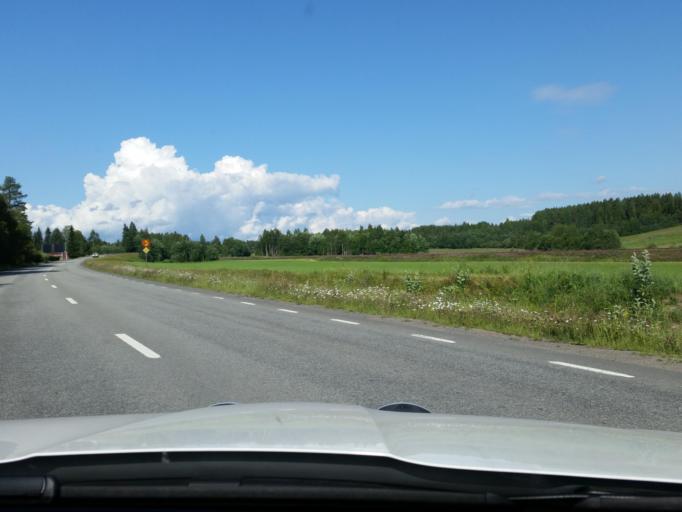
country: SE
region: Norrbotten
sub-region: Alvsbyns Kommun
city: AElvsbyn
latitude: 65.6667
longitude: 20.8911
